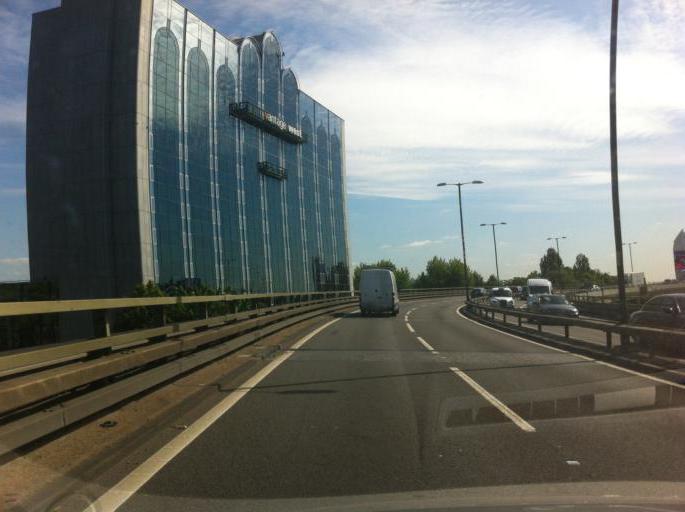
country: GB
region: England
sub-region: Greater London
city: Brentford
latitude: 51.4918
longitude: -0.2904
